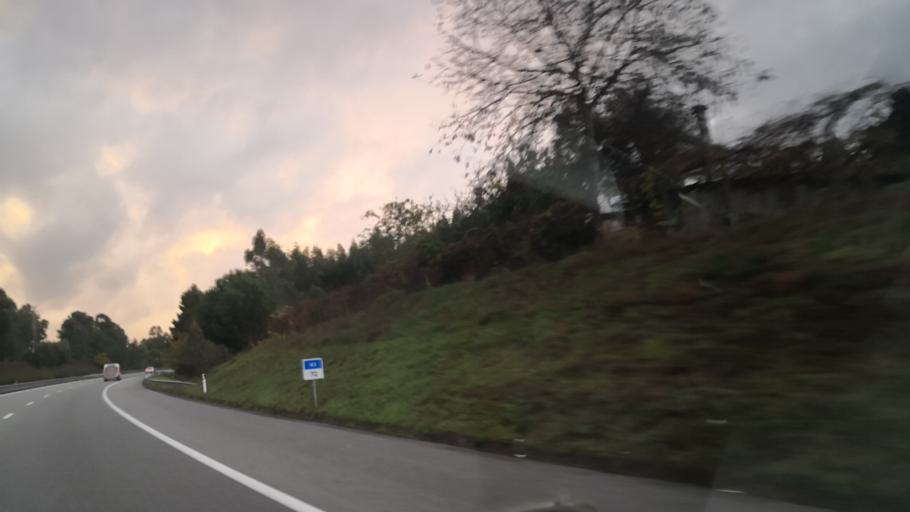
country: PT
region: Viana do Castelo
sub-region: Ponte de Lima
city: Ponte de Lima
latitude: 41.7285
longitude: -8.5612
